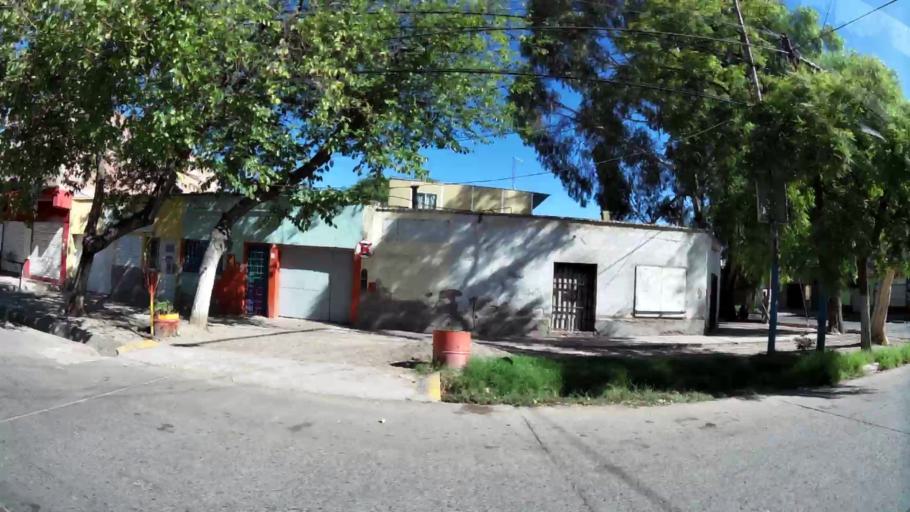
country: AR
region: Mendoza
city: Las Heras
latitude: -32.8424
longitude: -68.8090
